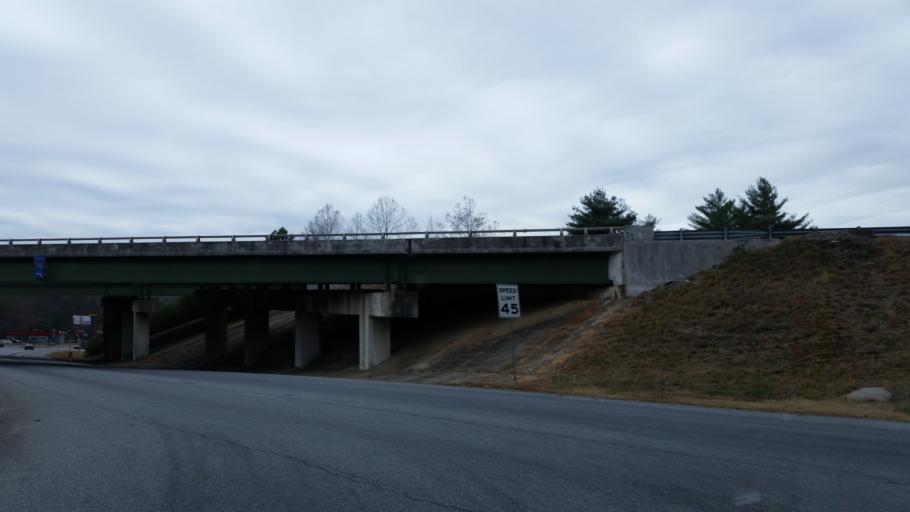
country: US
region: Georgia
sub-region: Bartow County
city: Cartersville
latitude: 34.2073
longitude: -84.7609
